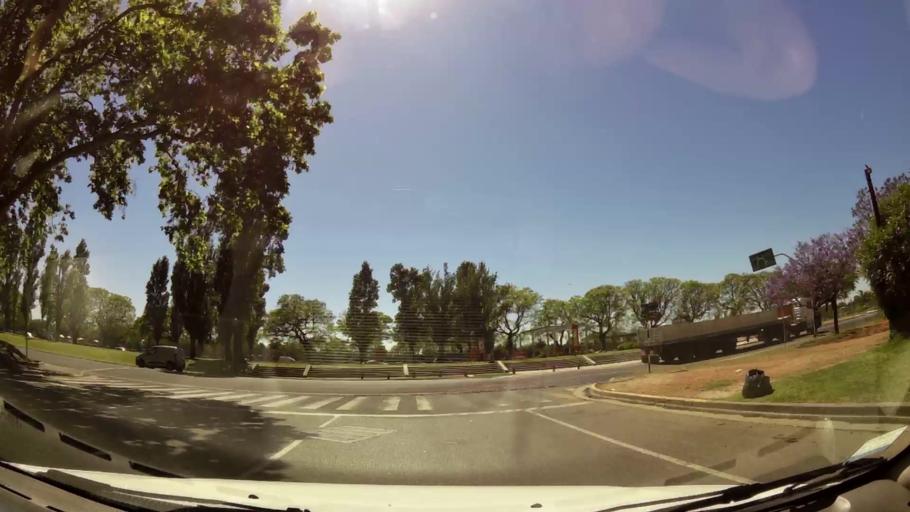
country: AR
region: Buenos Aires F.D.
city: Buenos Aires
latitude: -34.6107
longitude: -58.3596
